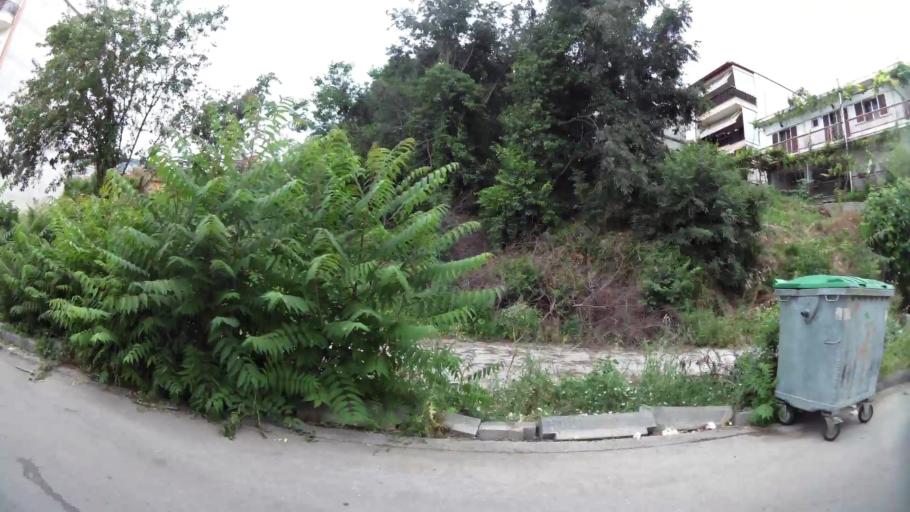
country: GR
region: Central Macedonia
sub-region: Nomos Imathias
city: Veroia
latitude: 40.5210
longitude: 22.2105
